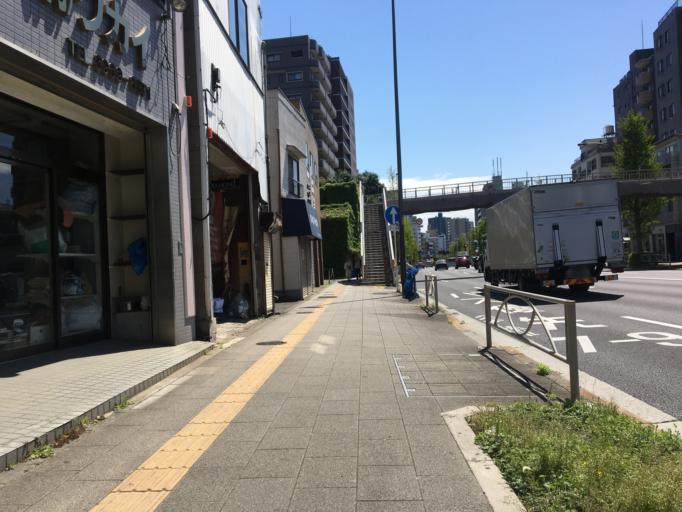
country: JP
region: Saitama
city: Kawaguchi
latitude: 35.7701
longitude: 139.7014
